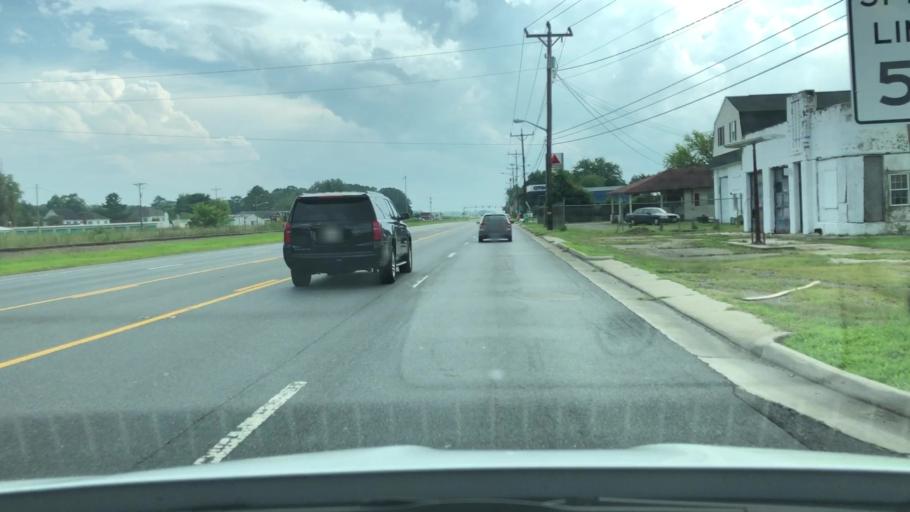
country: US
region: Virginia
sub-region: Northampton County
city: Exmore
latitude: 37.5893
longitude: -75.7828
